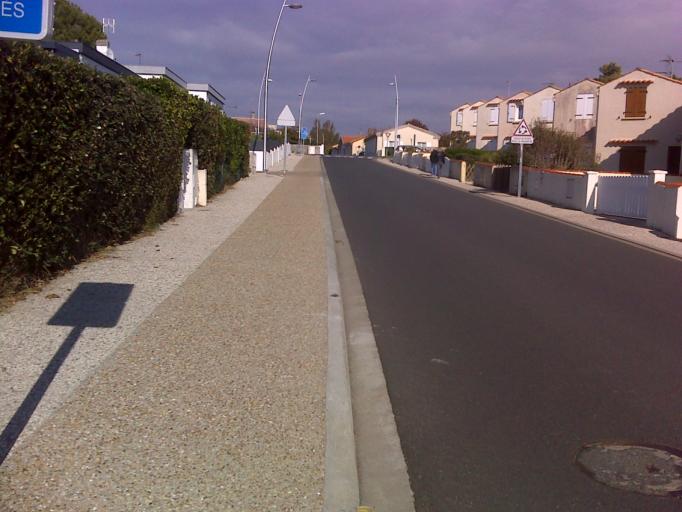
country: FR
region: Poitou-Charentes
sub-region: Departement de la Charente-Maritime
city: Vaux-sur-Mer
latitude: 45.6314
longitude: -1.0642
